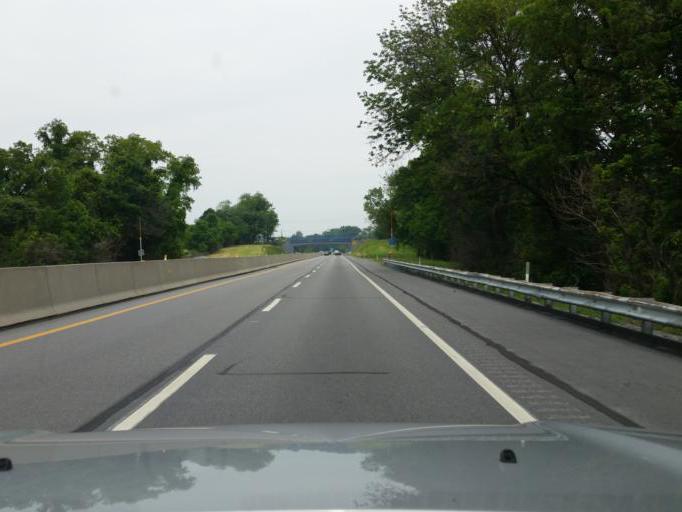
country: US
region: Pennsylvania
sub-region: Cumberland County
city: Shiremanstown
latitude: 40.1972
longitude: -76.9358
